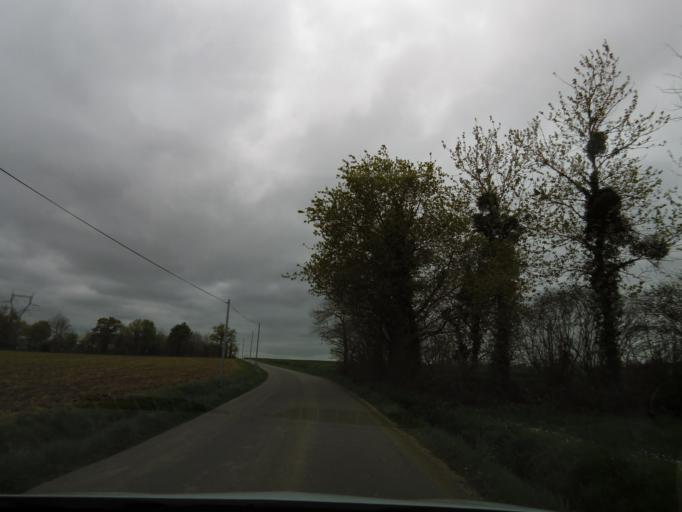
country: FR
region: Brittany
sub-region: Departement d'Ille-et-Vilaine
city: Janze
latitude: 47.9909
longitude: -1.5276
